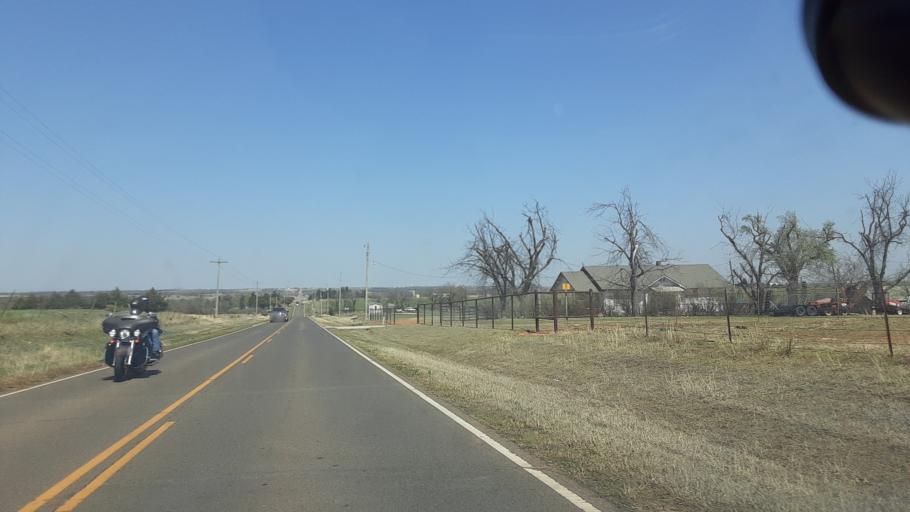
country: US
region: Oklahoma
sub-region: Logan County
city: Guthrie
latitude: 35.7920
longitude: -97.4784
